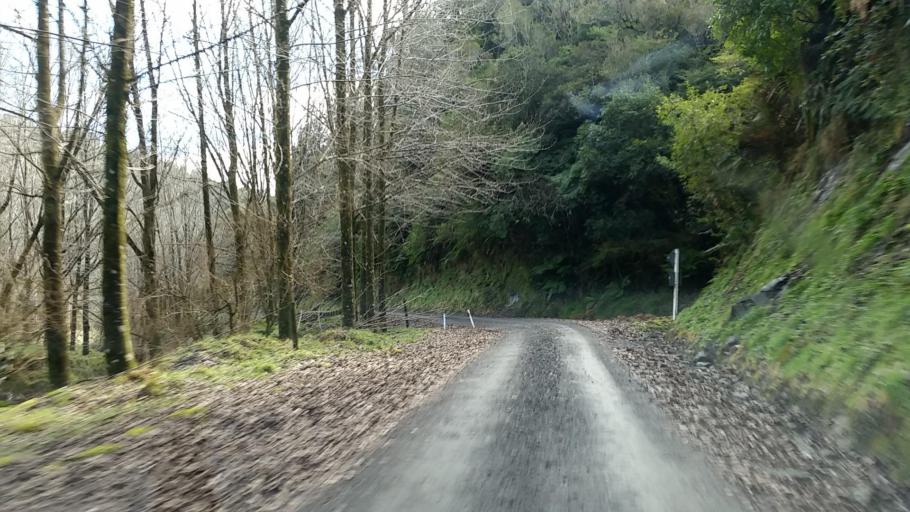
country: NZ
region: Taranaki
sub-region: New Plymouth District
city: Waitara
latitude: -39.1097
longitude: 174.5719
